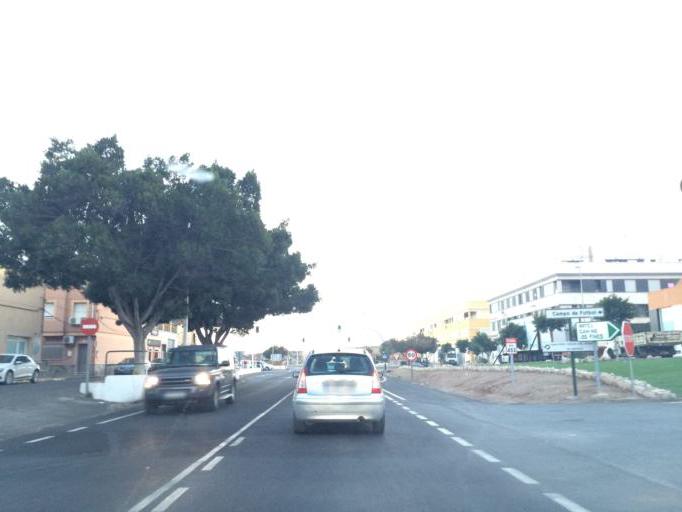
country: ES
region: Andalusia
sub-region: Provincia de Almeria
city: Benahadux
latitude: 36.9240
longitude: -2.4616
